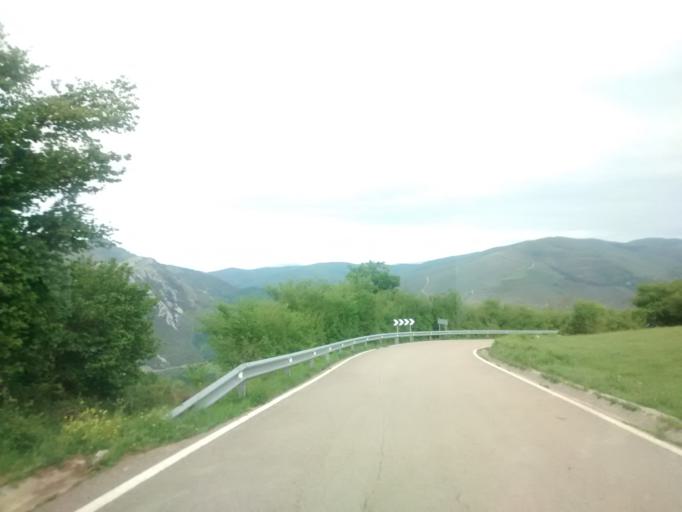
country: ES
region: Cantabria
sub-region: Provincia de Cantabria
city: San Vicente de la Barquera
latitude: 43.2569
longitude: -4.4415
